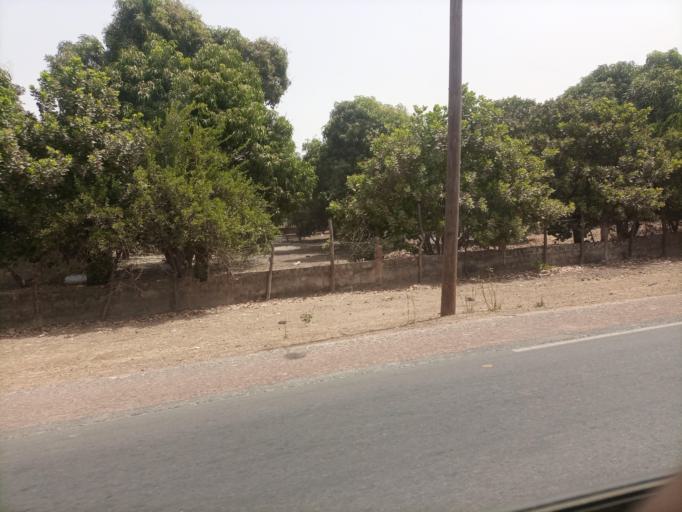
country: SN
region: Fatick
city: Sokone
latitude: 13.7377
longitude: -16.4259
